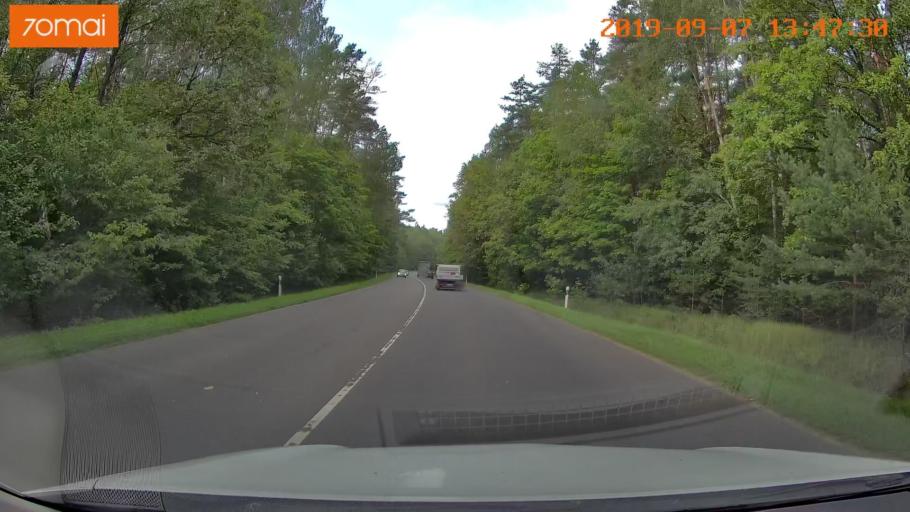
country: LT
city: Baltoji Voke
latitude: 54.5977
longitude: 25.2139
